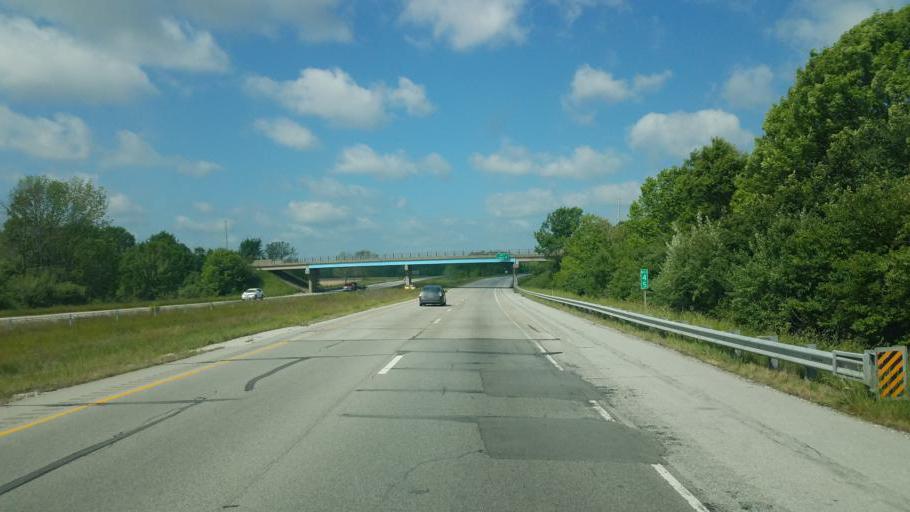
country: US
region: Indiana
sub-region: Putnam County
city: Cloverdale
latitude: 39.5450
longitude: -86.7328
